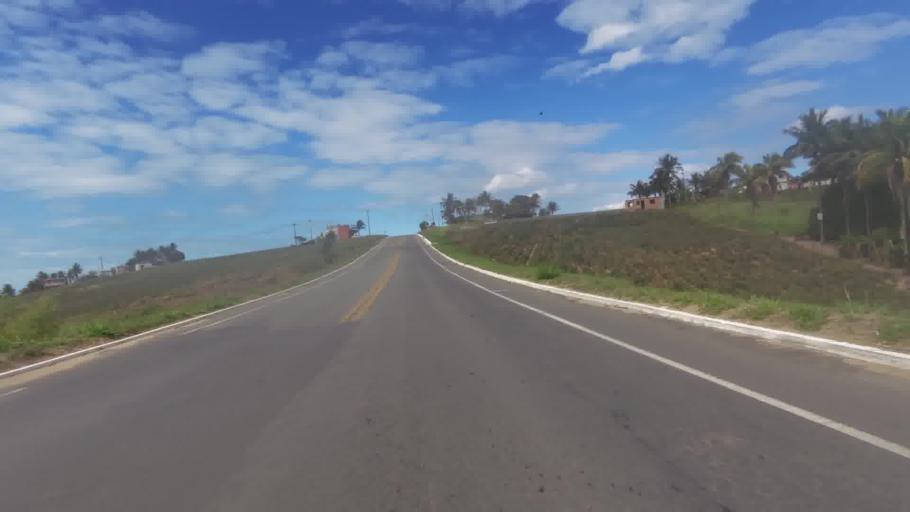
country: BR
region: Espirito Santo
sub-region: Marataizes
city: Marataizes
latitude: -21.0591
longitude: -40.8492
